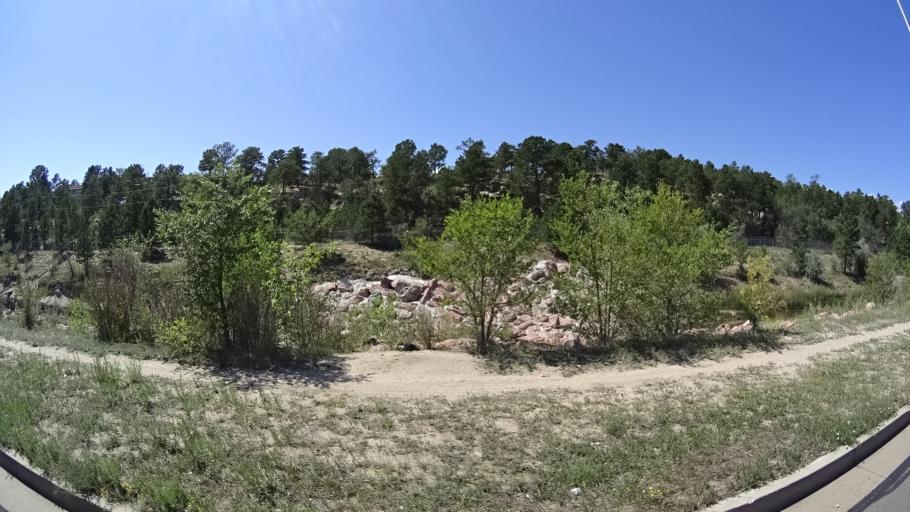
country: US
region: Colorado
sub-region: El Paso County
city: Cimarron Hills
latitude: 38.8529
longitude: -104.7234
